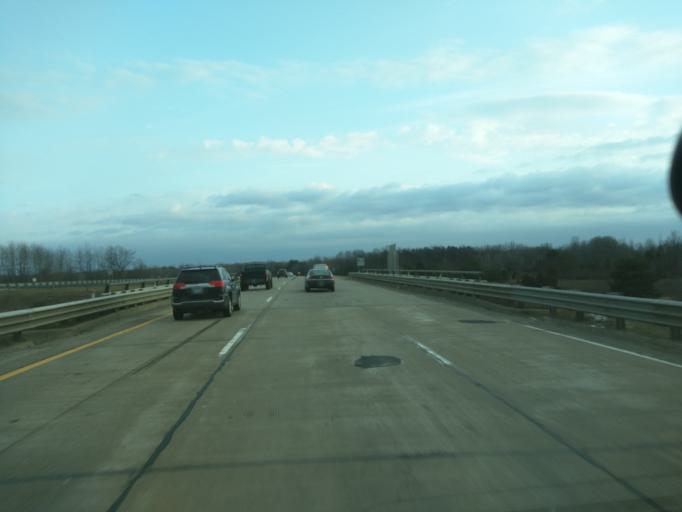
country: US
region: Michigan
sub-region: Ingham County
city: Holt
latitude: 42.6750
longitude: -84.4959
